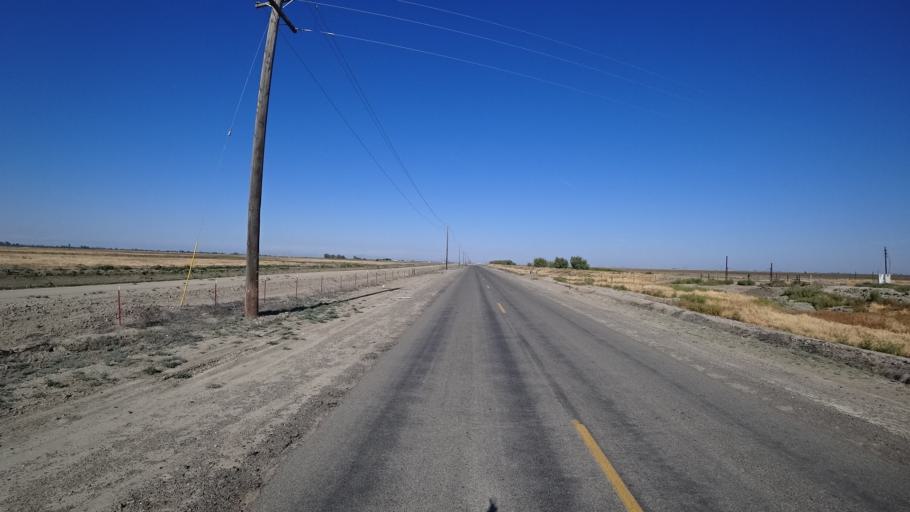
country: US
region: California
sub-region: Kings County
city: Corcoran
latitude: 36.1379
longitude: -119.5407
